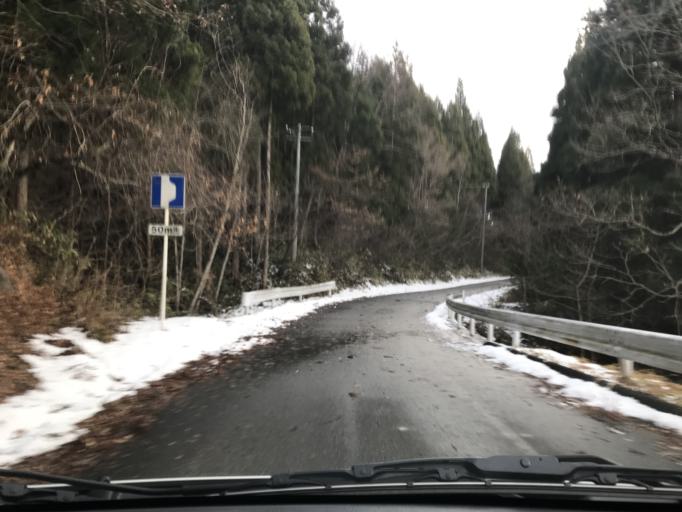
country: JP
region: Iwate
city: Ichinoseki
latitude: 39.0132
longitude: 140.9764
